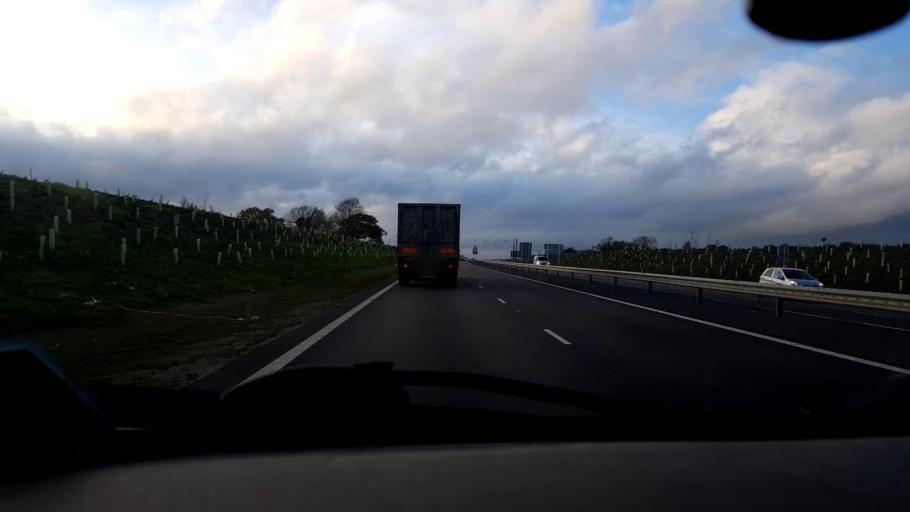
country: GB
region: England
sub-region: Norfolk
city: Horsford
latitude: 52.6834
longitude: 1.2508
